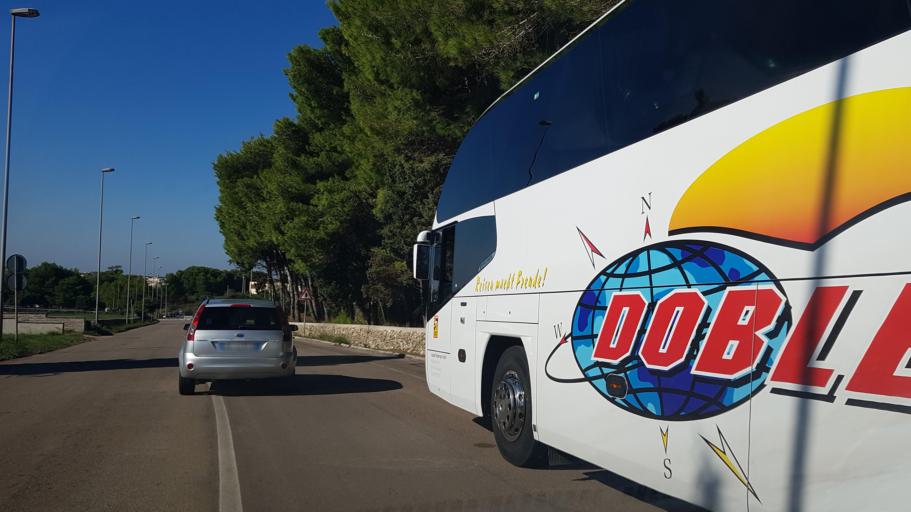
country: IT
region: Apulia
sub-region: Provincia di Lecce
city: Otranto
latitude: 40.1407
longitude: 18.4991
